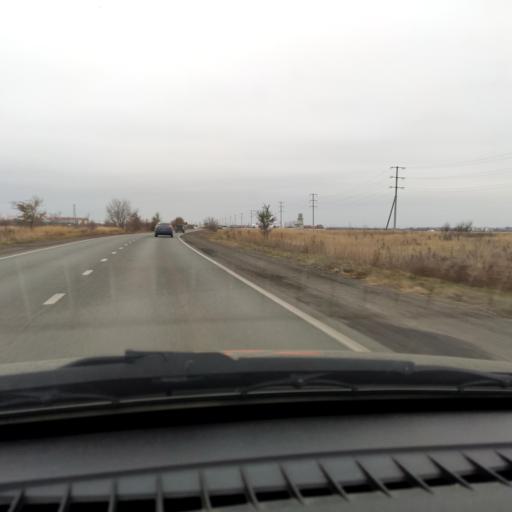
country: RU
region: Samara
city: Podstepki
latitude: 53.5193
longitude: 49.2064
